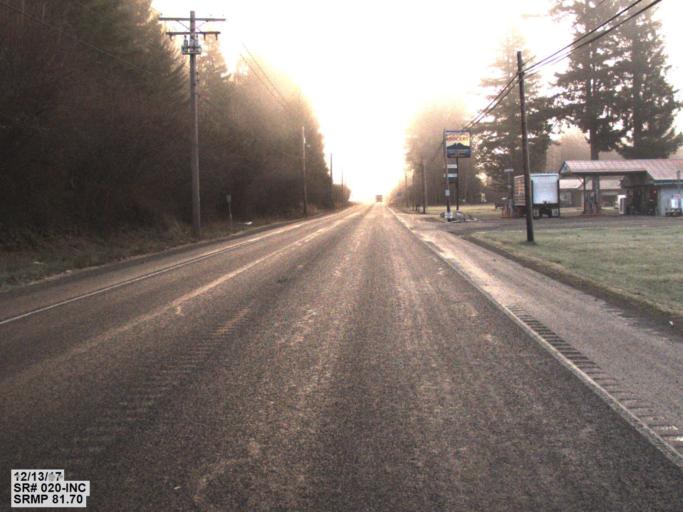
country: US
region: Washington
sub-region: Skagit County
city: Sedro-Woolley
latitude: 48.5300
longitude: -121.8998
